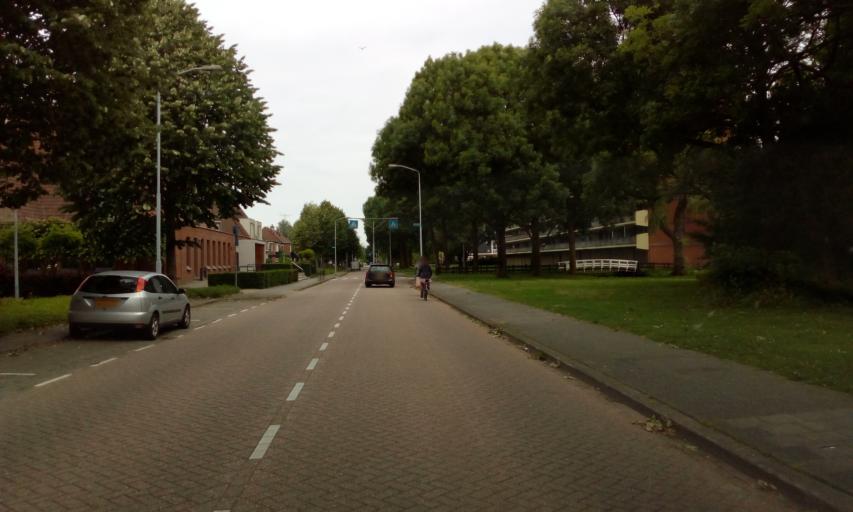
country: NL
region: South Holland
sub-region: Gemeente Alblasserdam
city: Alblasserdam
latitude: 51.8681
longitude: 4.6661
